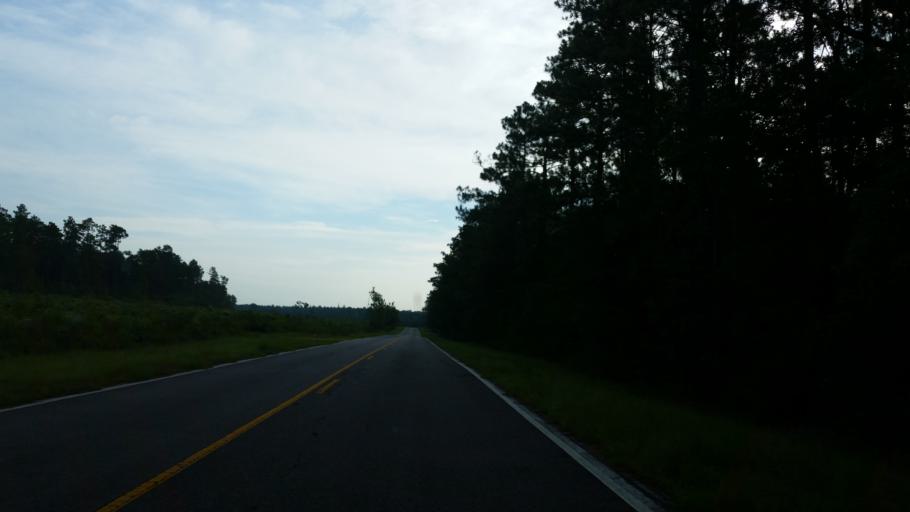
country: US
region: Florida
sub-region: Escambia County
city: Molino
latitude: 30.7702
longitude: -87.5010
